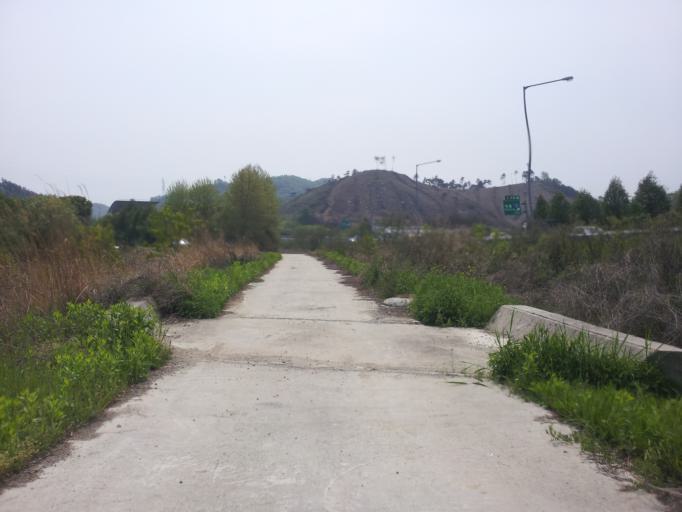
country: KR
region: Daejeon
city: Daejeon
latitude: 36.2587
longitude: 127.2819
